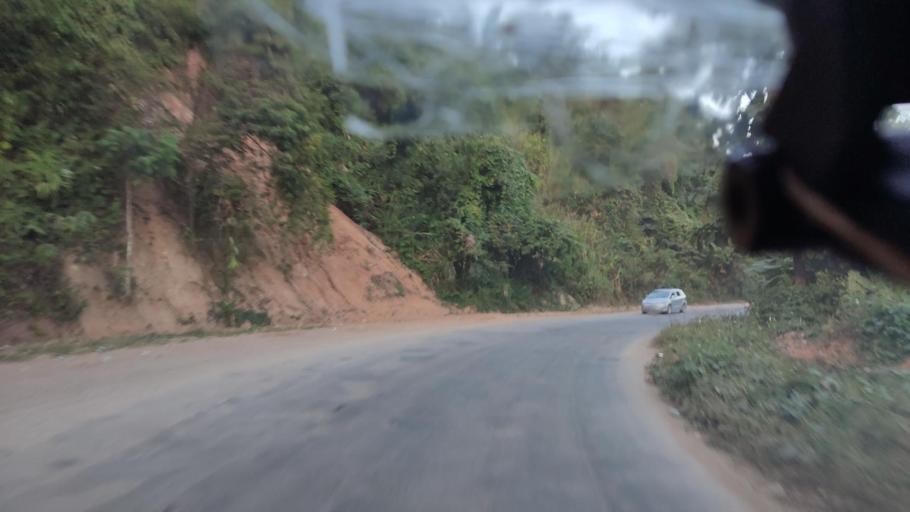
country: TH
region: Chiang Rai
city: Mae Sai
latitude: 20.8672
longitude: 99.8997
